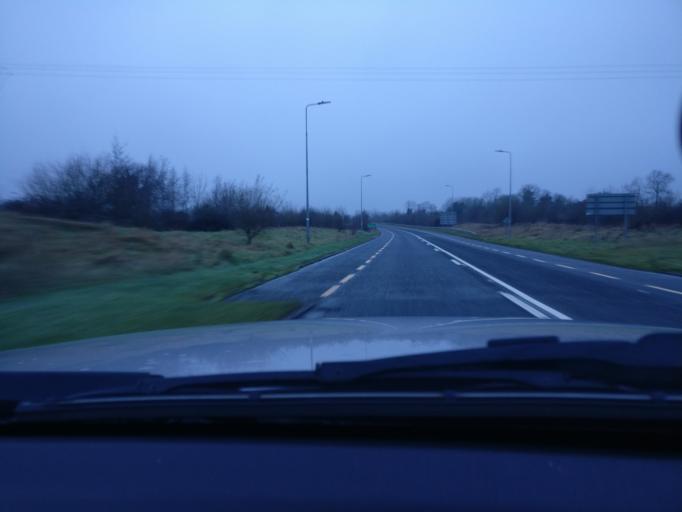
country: IE
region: Leinster
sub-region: An Iarmhi
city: Rochfortbridge
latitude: 53.3929
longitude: -7.3699
